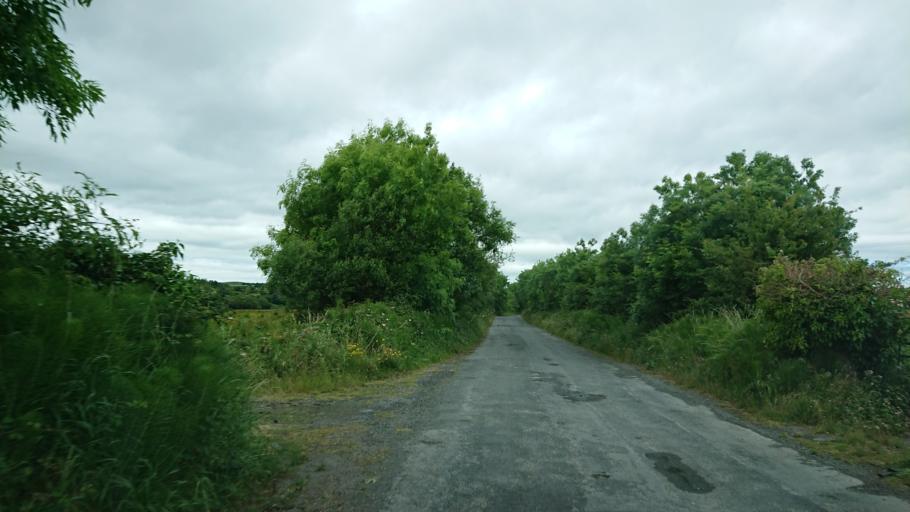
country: IE
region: Munster
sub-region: Waterford
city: Waterford
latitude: 52.2214
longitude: -7.1430
